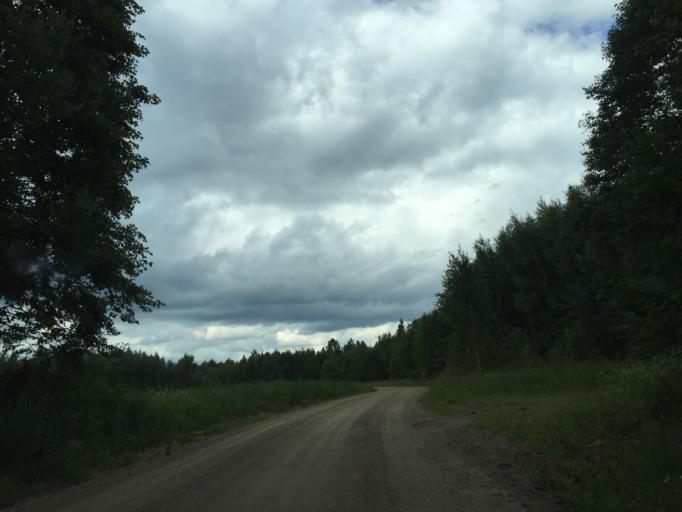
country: LV
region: Malpils
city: Malpils
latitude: 56.8999
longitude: 24.9860
